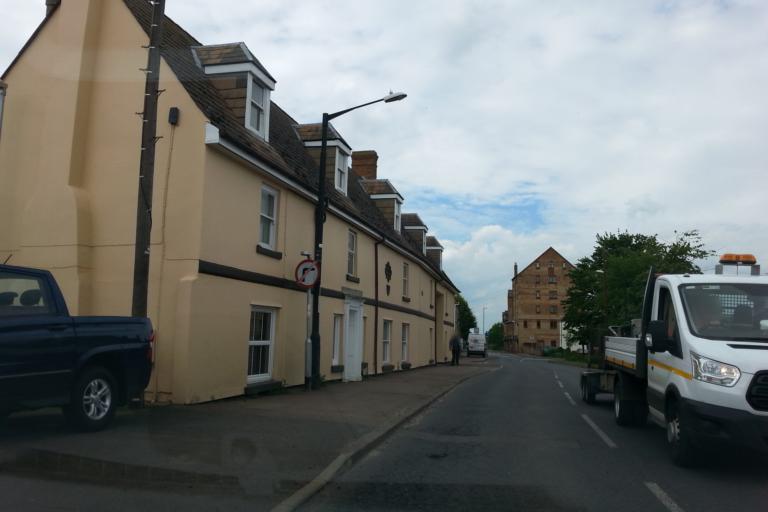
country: GB
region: England
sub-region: Cambridgeshire
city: Ramsey
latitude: 52.4524
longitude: -0.1101
